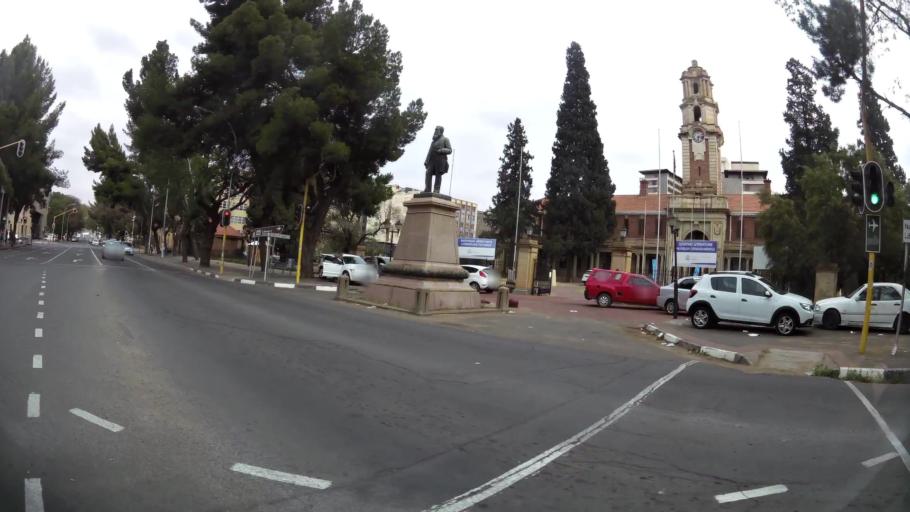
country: ZA
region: Orange Free State
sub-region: Mangaung Metropolitan Municipality
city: Bloemfontein
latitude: -29.1167
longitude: 26.2169
